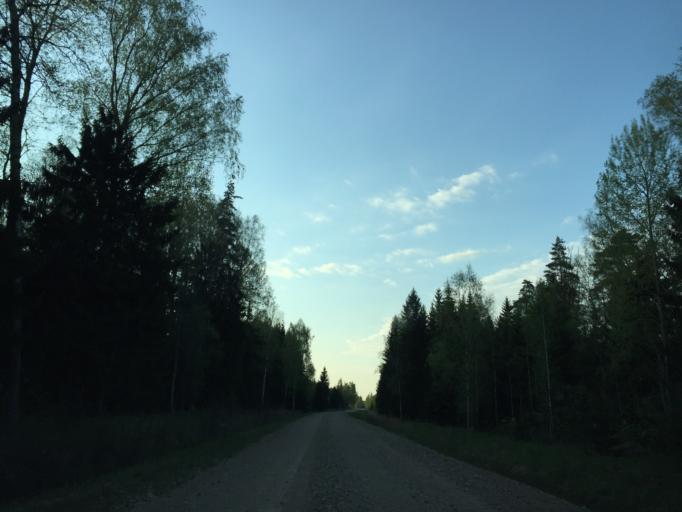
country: LV
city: Tireli
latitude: 56.8475
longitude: 23.6958
